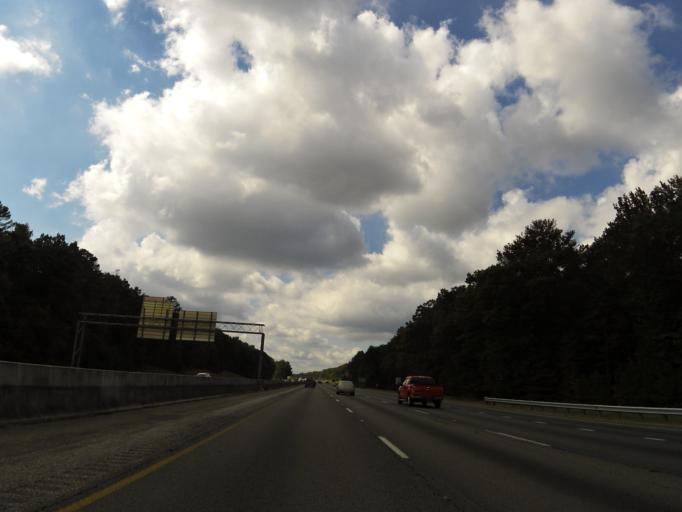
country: US
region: Alabama
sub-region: Tuscaloosa County
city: Lake View
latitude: 33.3302
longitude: -87.0412
